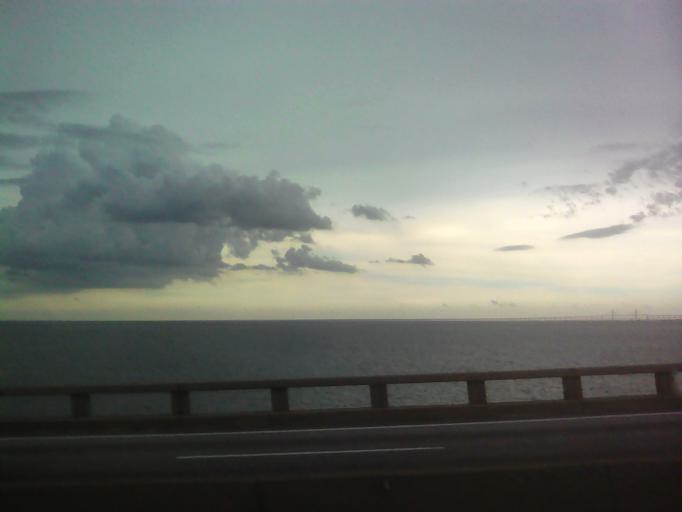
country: MY
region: Perak
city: Ipoh
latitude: 4.6083
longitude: 101.0706
